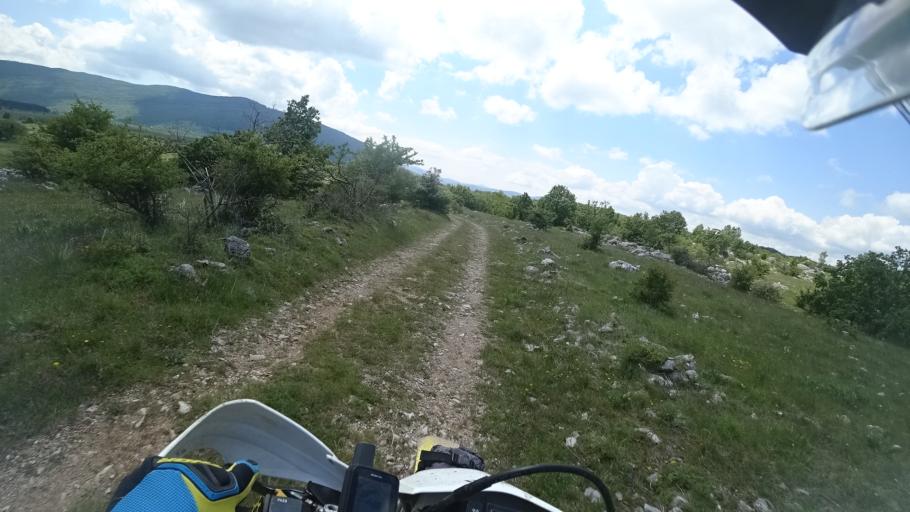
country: HR
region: Zadarska
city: Gracac
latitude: 44.3636
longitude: 15.9457
